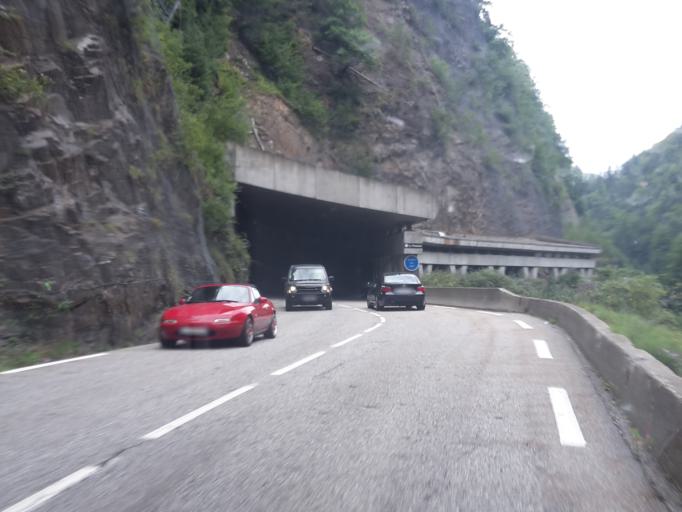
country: FR
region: Rhone-Alpes
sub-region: Departement de la Savoie
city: Ugine
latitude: 45.7844
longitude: 6.4849
